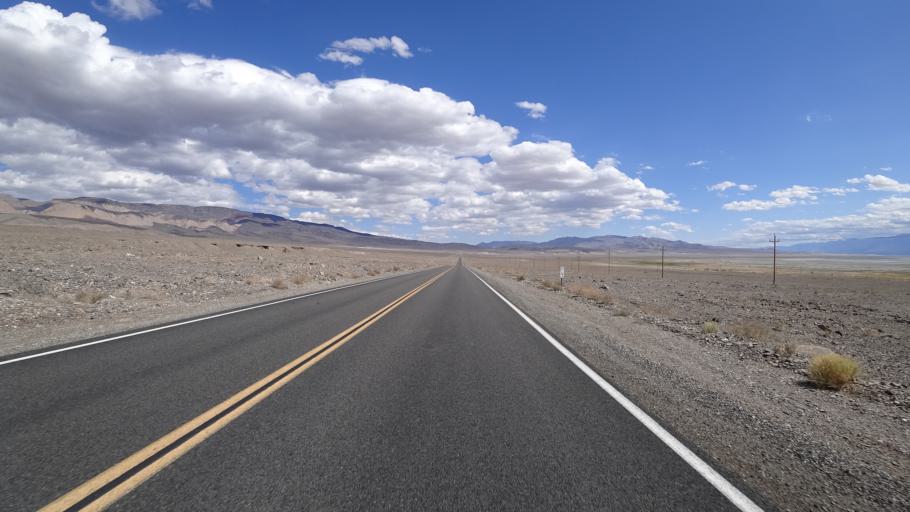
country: US
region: California
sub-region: Inyo County
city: Lone Pine
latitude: 36.4644
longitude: -117.8488
